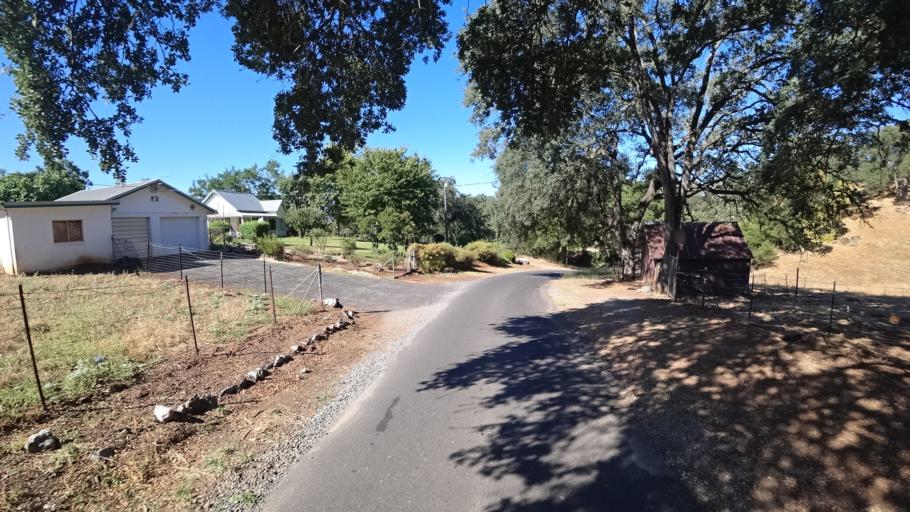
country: US
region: California
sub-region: Calaveras County
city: San Andreas
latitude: 38.2237
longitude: -120.6807
